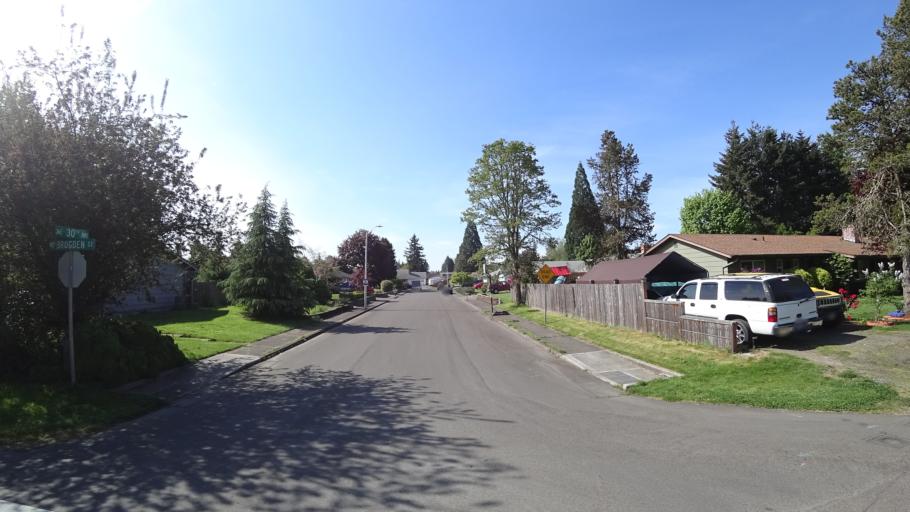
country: US
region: Oregon
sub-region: Washington County
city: Hillsboro
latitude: 45.5243
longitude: -122.9523
